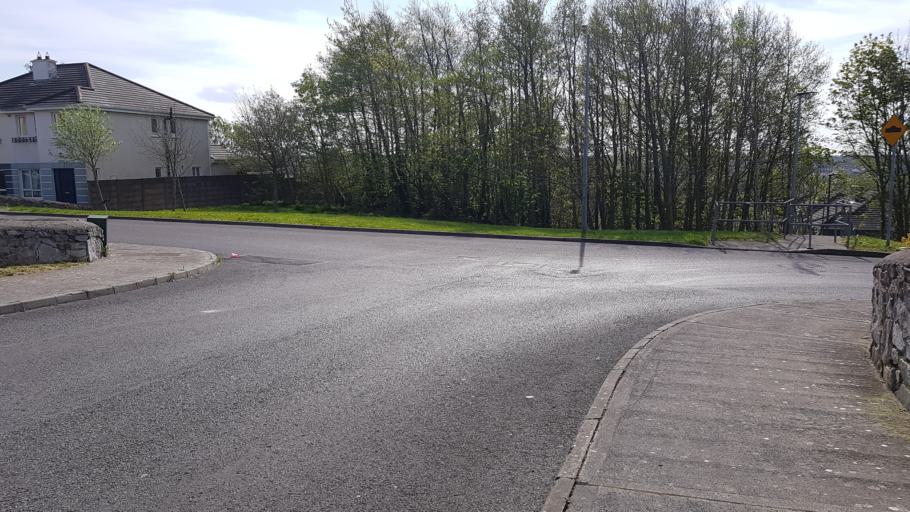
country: IE
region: Connaught
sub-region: County Galway
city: Gaillimh
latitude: 53.2946
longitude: -9.0396
